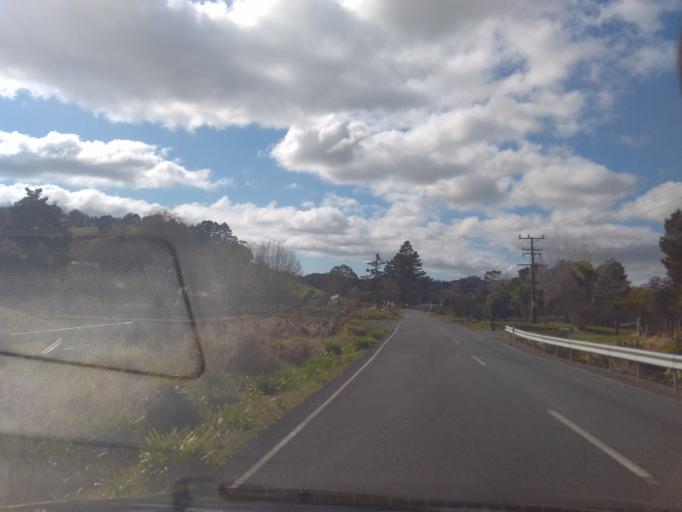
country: NZ
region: Northland
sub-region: Whangarei
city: Whangarei
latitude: -35.7010
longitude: 174.3495
